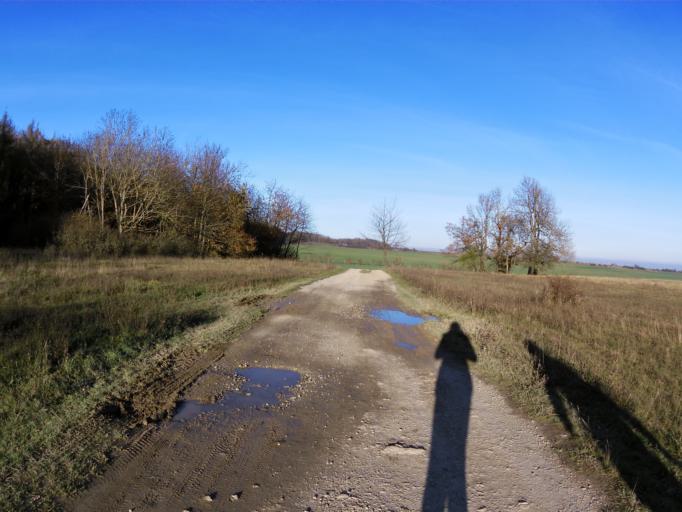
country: DE
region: Thuringia
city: Weberstedt
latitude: 51.0622
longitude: 10.4568
